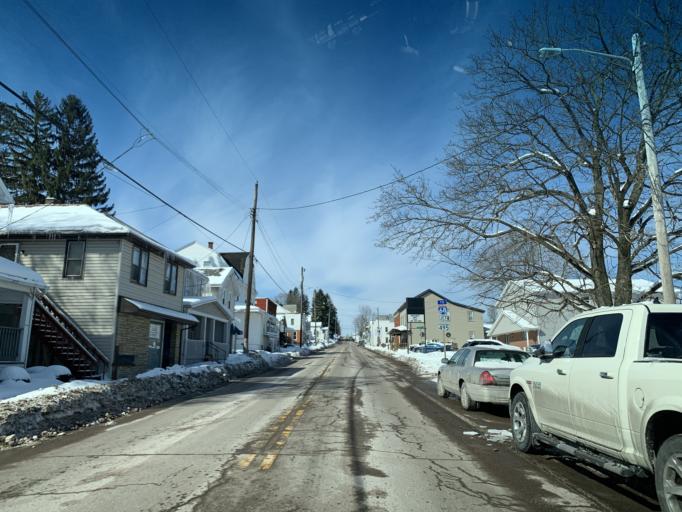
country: US
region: Pennsylvania
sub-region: Somerset County
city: Meyersdale
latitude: 39.6965
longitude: -79.1550
